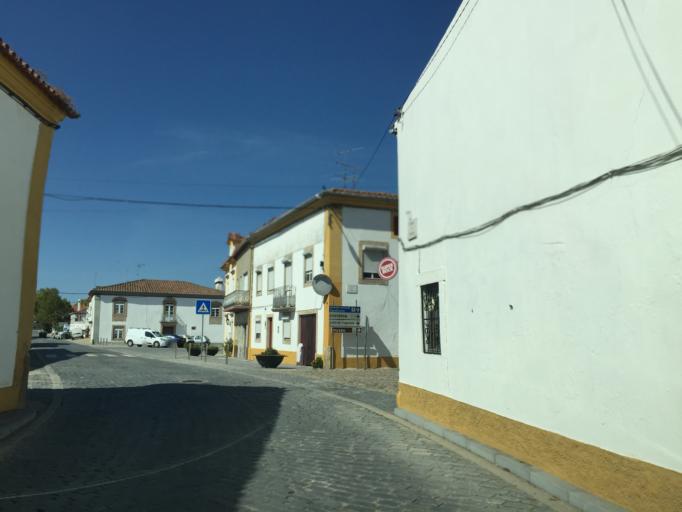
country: PT
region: Portalegre
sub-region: Portalegre
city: Alagoa
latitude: 39.4157
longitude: -7.6170
